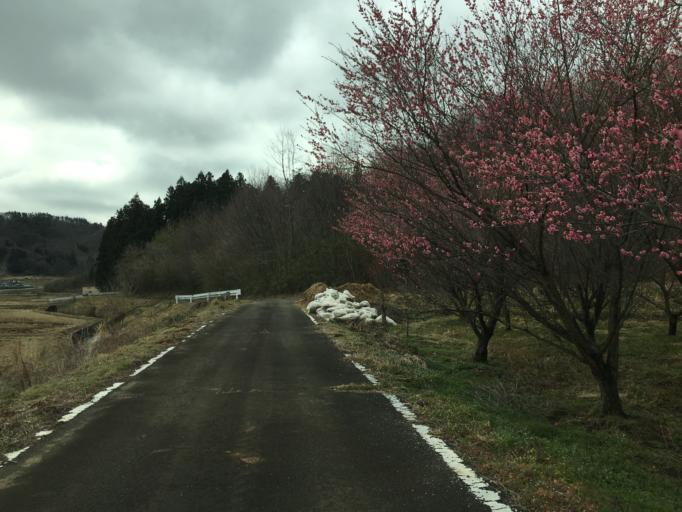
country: JP
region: Fukushima
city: Fukushima-shi
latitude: 37.7036
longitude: 140.4190
